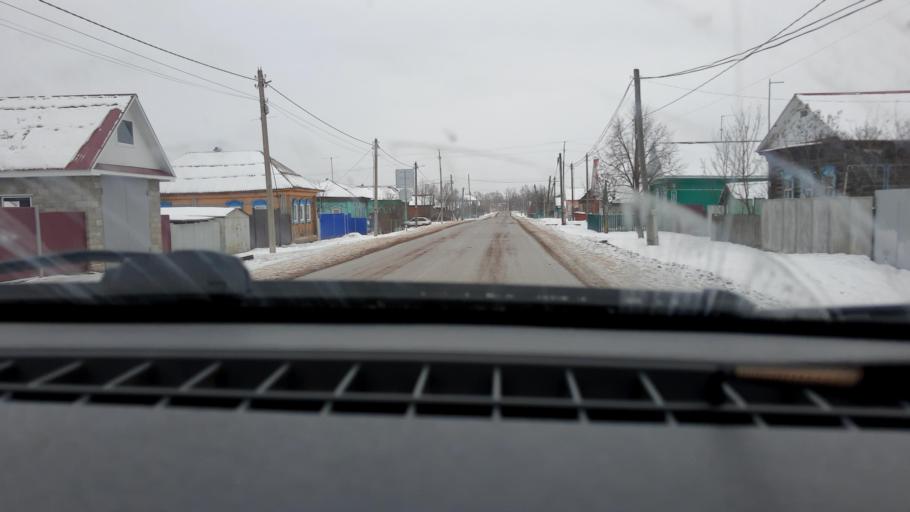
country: RU
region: Bashkortostan
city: Kabakovo
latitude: 54.7026
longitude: 56.2514
